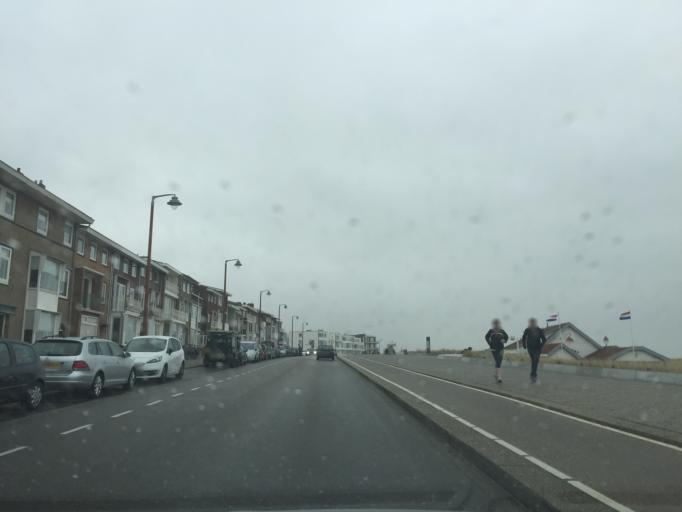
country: NL
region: South Holland
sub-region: Gemeente Katwijk
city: Katwijk aan Zee
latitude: 52.2021
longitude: 4.3917
